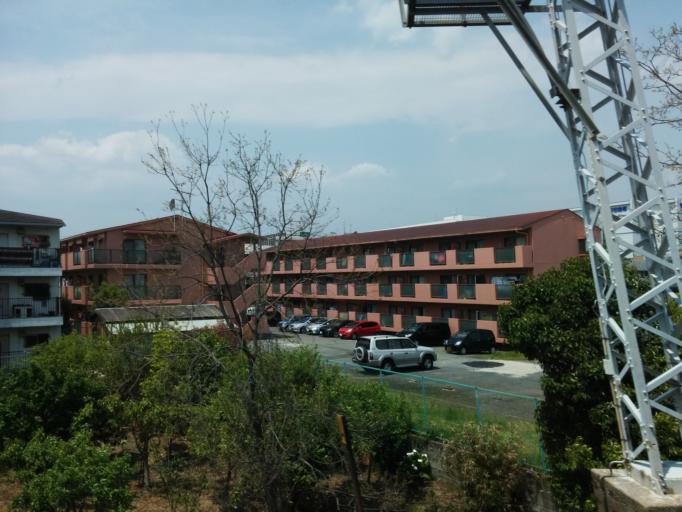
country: JP
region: Osaka
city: Ibaraki
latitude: 34.7968
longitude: 135.5612
